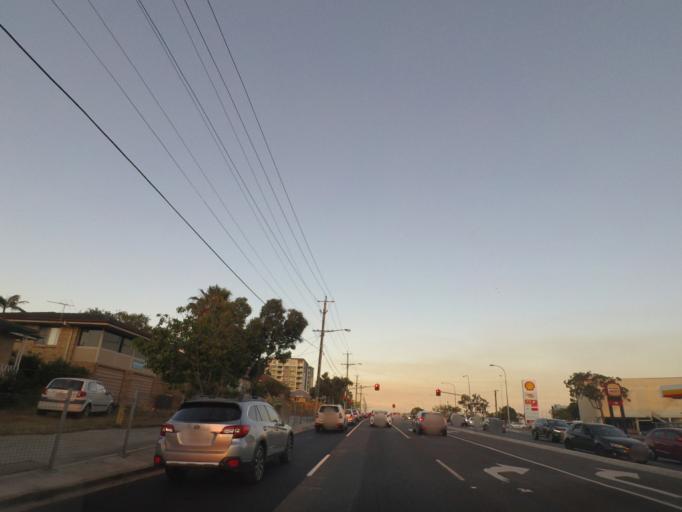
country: AU
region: Queensland
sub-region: Brisbane
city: Upper Mount Gravatt
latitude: -27.5607
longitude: 153.0783
